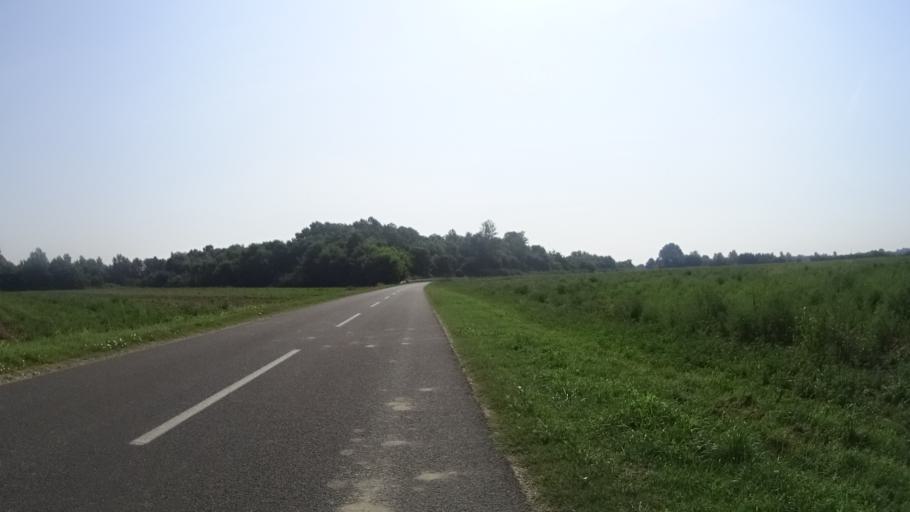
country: HR
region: Medimurska
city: Belica
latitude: 46.3949
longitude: 16.5272
